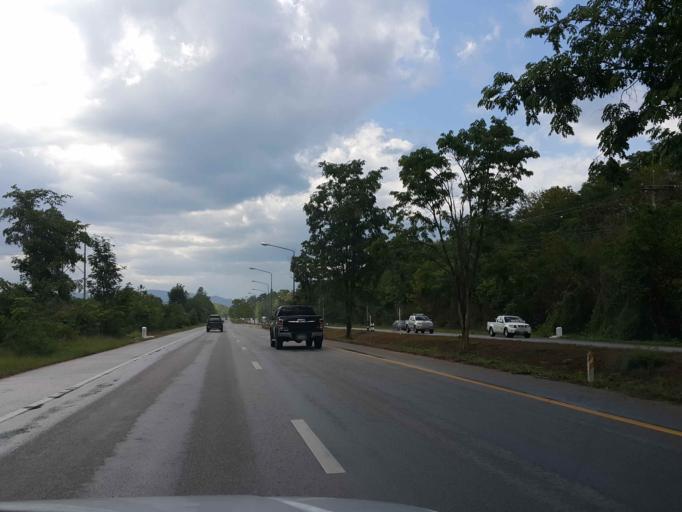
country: TH
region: Lampang
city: Thoen
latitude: 17.6739
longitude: 99.2435
